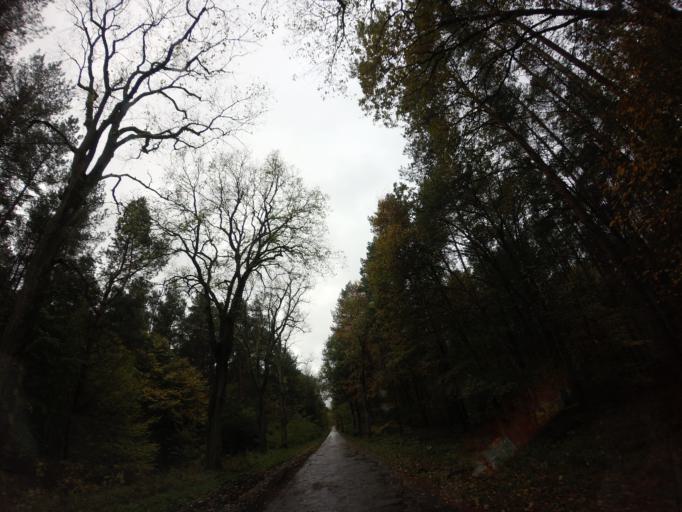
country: PL
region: West Pomeranian Voivodeship
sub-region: Powiat choszczenski
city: Krzecin
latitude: 53.0302
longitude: 15.5357
